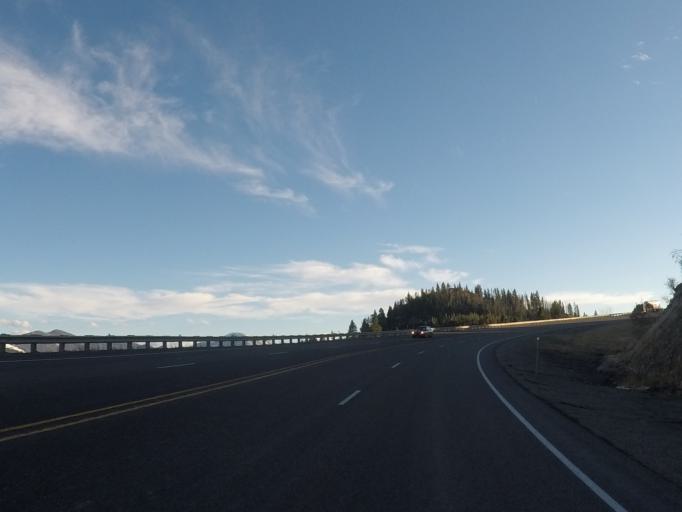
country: US
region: Montana
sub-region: Lewis and Clark County
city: Helena West Side
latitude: 46.5842
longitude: -112.2681
